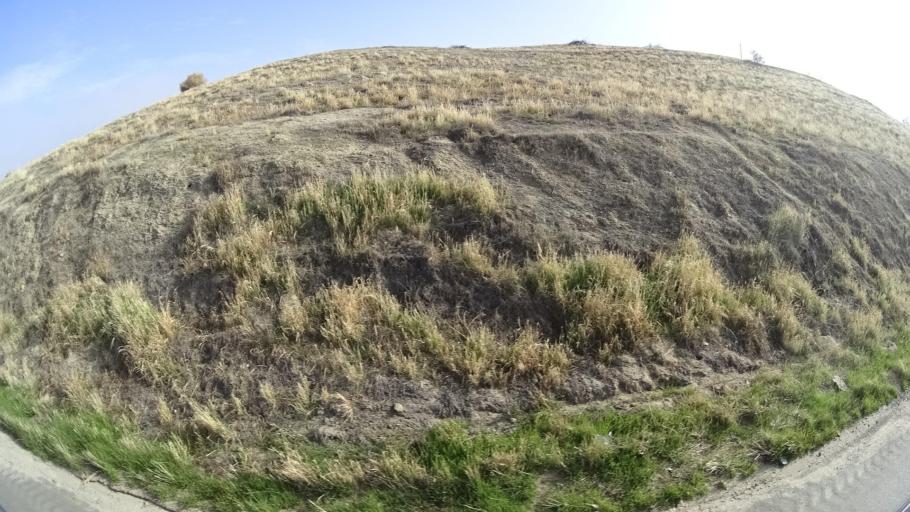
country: US
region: California
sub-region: Kern County
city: Ford City
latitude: 35.1658
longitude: -119.4210
